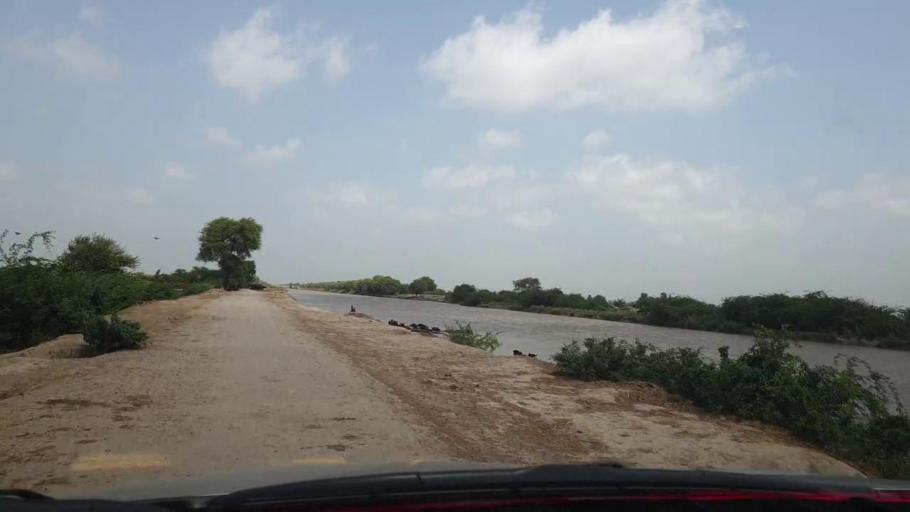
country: PK
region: Sindh
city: Talhar
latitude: 24.8944
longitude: 68.8356
